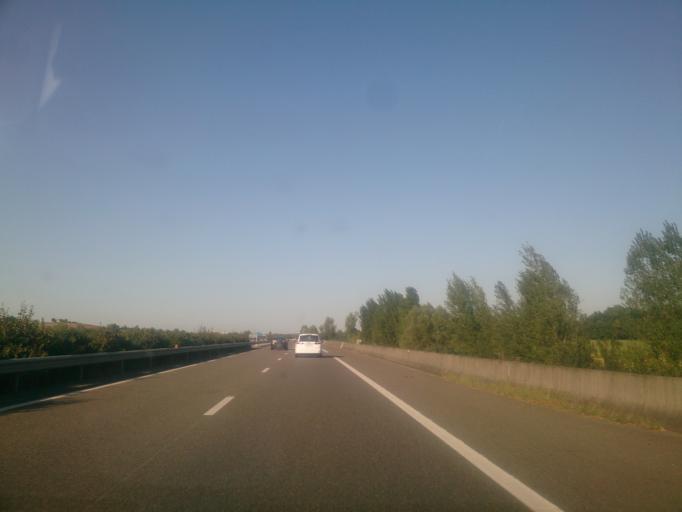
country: FR
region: Midi-Pyrenees
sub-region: Departement du Tarn-et-Garonne
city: Caussade
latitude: 44.1452
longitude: 1.5050
